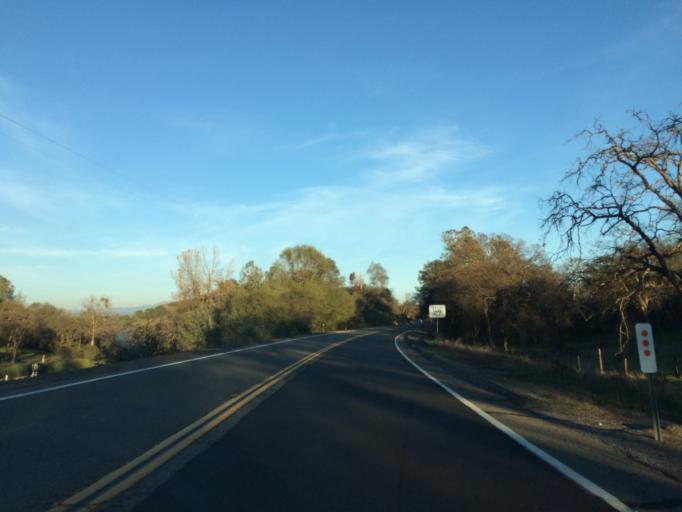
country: US
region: California
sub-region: Mariposa County
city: Mariposa
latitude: 37.4791
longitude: -120.0641
